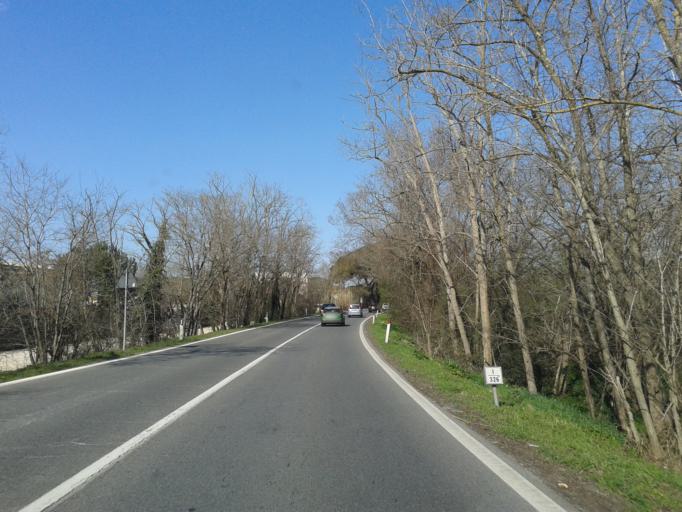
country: IT
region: Tuscany
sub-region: Province of Pisa
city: Marina di Pisa-Tirrenia-Calambrone
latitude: 43.6364
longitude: 10.3543
